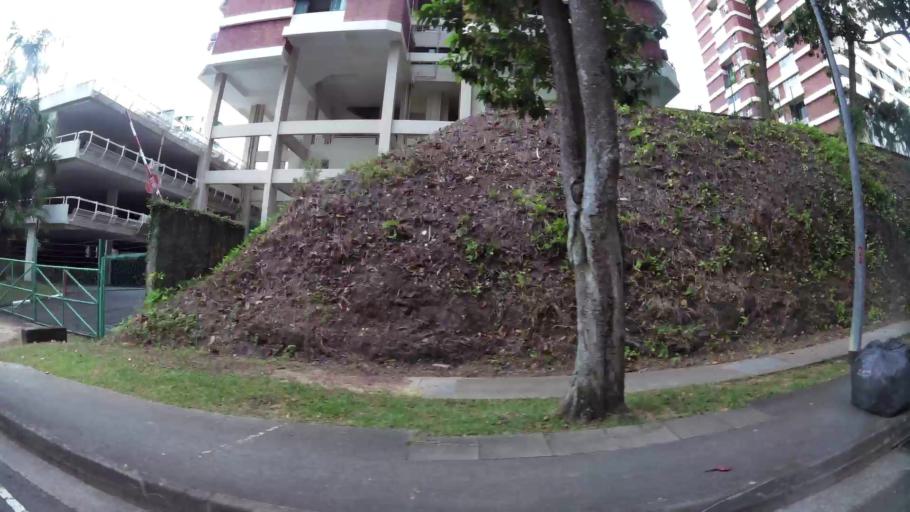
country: SG
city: Singapore
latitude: 1.3180
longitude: 103.7779
